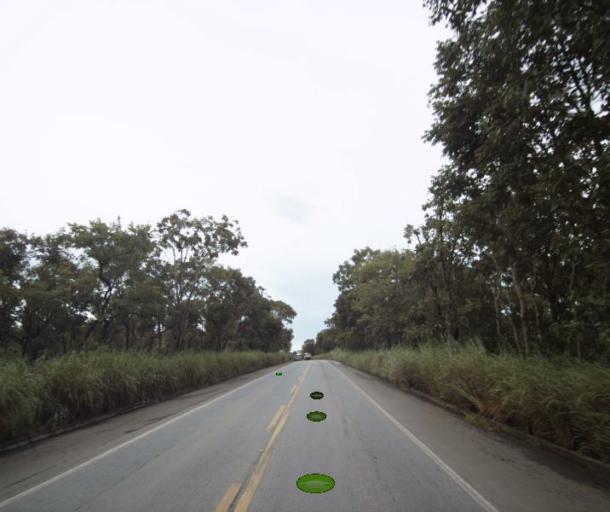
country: BR
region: Goias
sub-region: Porangatu
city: Porangatu
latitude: -13.6258
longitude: -49.0427
